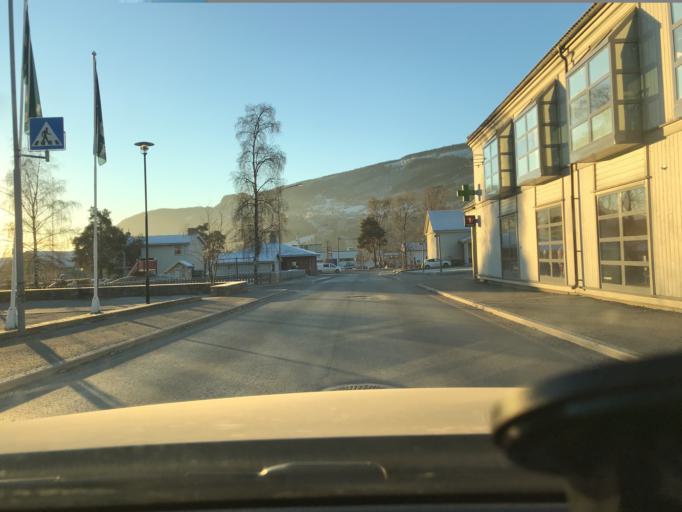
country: NO
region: Oppland
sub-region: Ringebu
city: Ringebu
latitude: 61.5305
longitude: 10.1406
